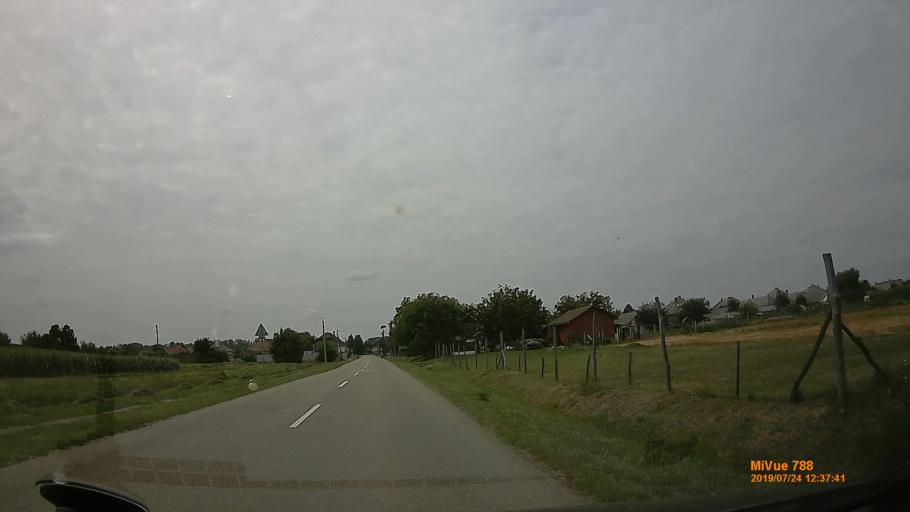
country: HU
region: Szabolcs-Szatmar-Bereg
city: Vasarosnameny
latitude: 48.1896
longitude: 22.3232
